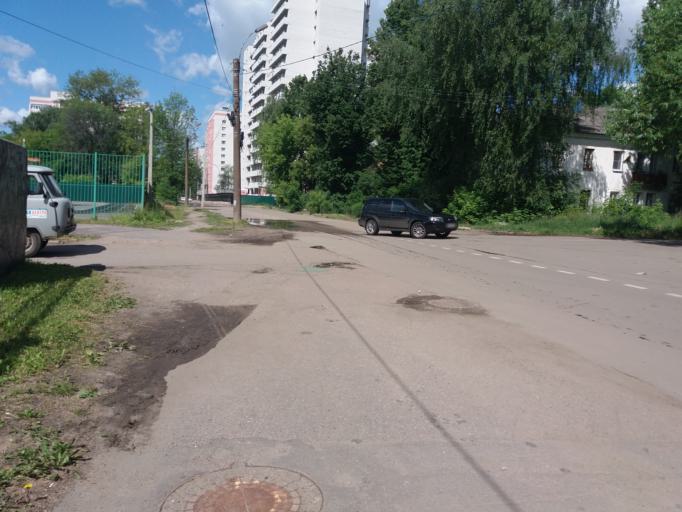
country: RU
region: Jaroslavl
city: Yaroslavl
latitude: 57.6404
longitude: 39.8479
